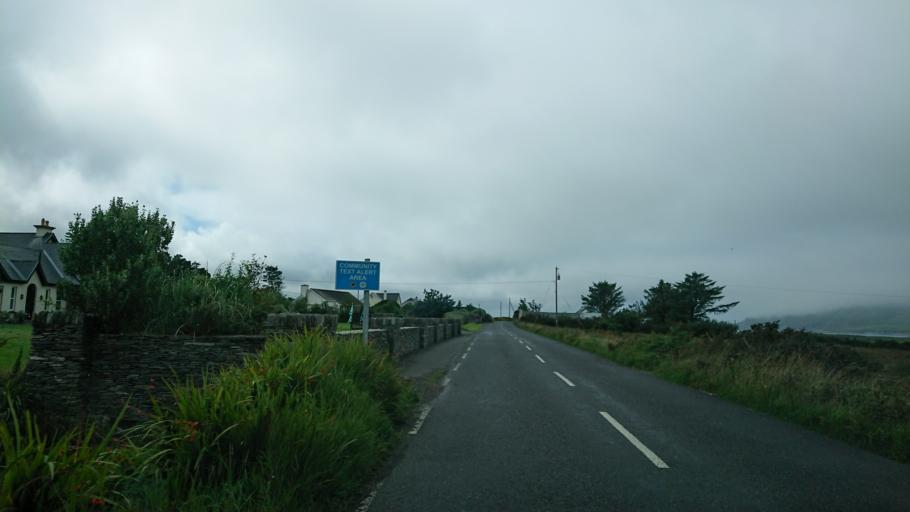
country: IE
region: Munster
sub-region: Ciarrai
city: Cahersiveen
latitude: 51.9327
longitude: -10.2544
